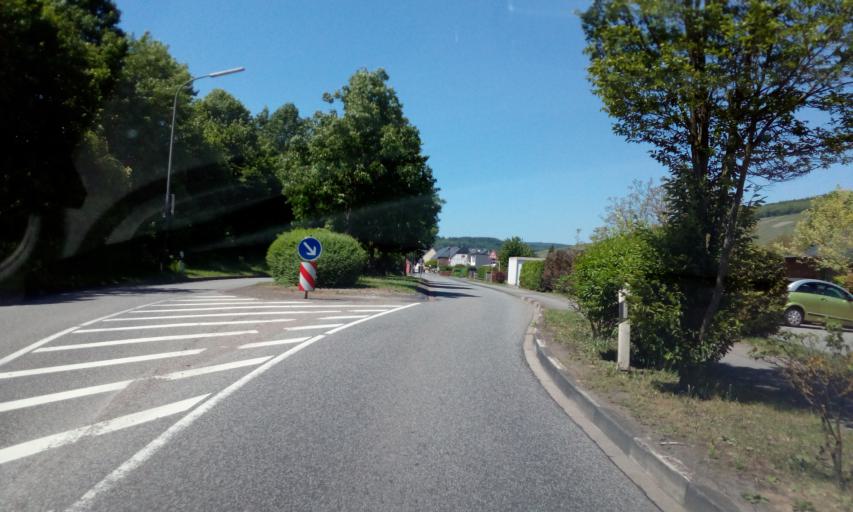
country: DE
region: Rheinland-Pfalz
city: Monzelfeld
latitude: 49.9077
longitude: 7.0472
